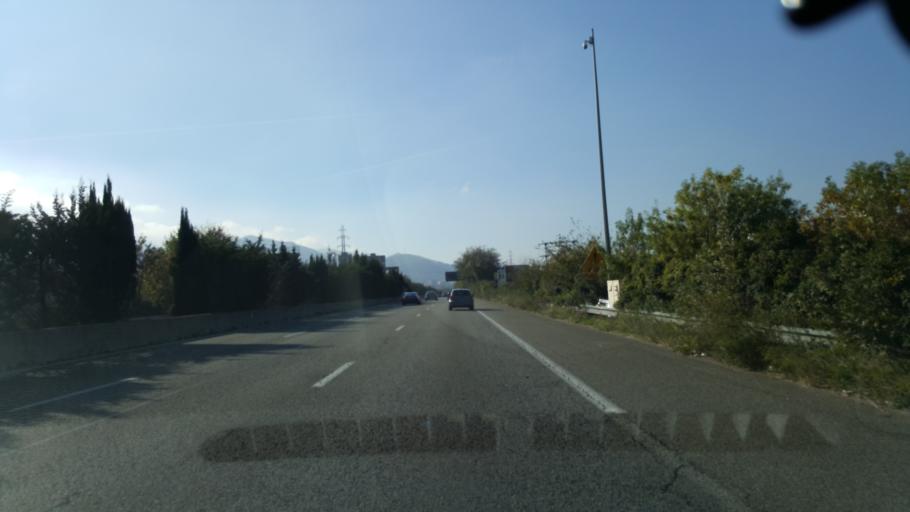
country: FR
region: Provence-Alpes-Cote d'Azur
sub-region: Departement des Bouches-du-Rhone
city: La Penne-sur-Huveaune
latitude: 43.2864
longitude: 5.5343
